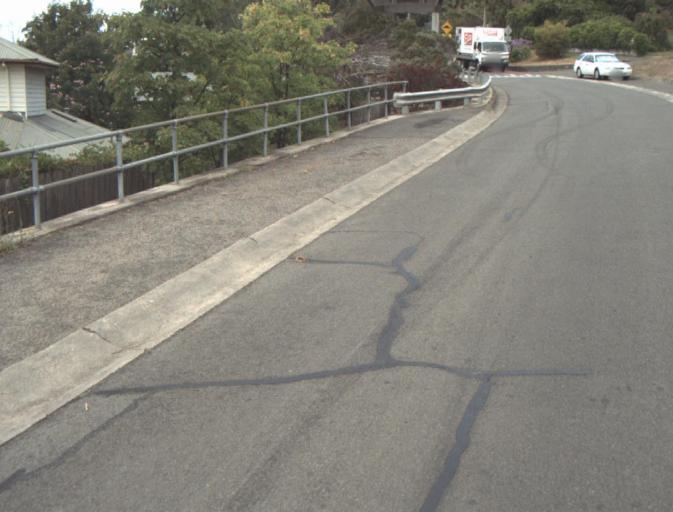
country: AU
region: Tasmania
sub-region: Launceston
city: Launceston
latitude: -41.4319
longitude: 147.1192
